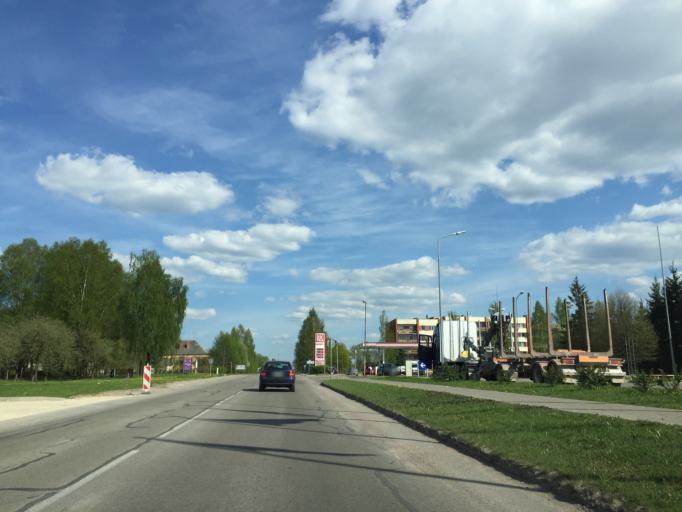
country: LV
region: Limbazu Rajons
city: Limbazi
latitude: 57.5128
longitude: 24.7279
